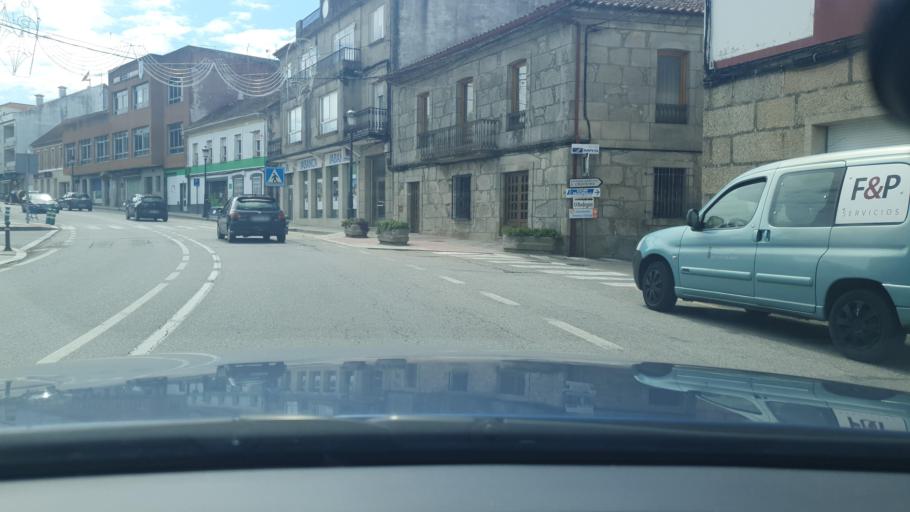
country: ES
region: Galicia
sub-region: Provincia de Pontevedra
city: Sanxenxo
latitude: 42.4430
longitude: -8.8358
